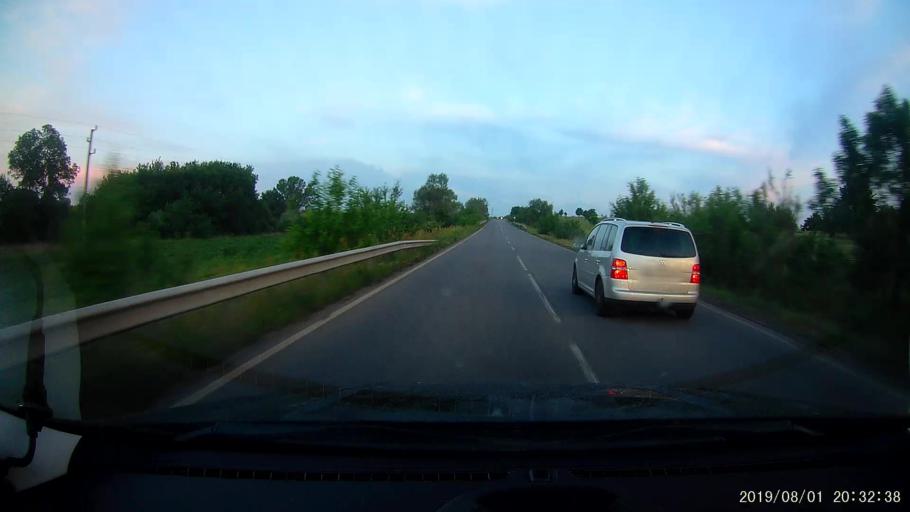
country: BG
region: Yambol
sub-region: Obshtina Elkhovo
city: Elkhovo
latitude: 42.1191
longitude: 26.5300
